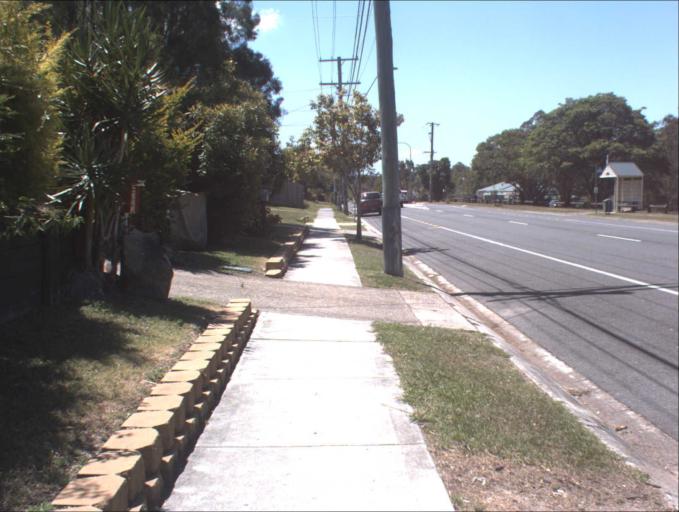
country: AU
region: Queensland
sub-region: Logan
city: Springwood
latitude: -27.6082
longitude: 153.1368
